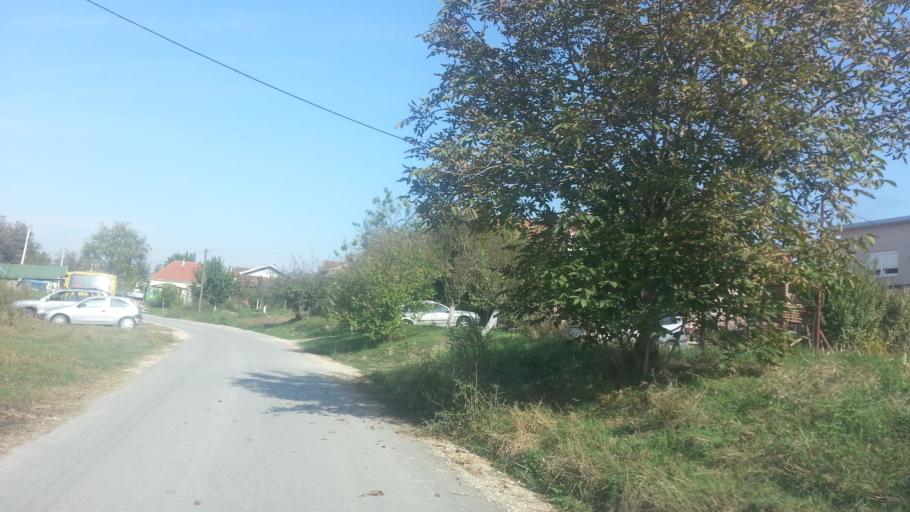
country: RS
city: Stari Banovci
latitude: 44.9958
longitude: 20.2789
